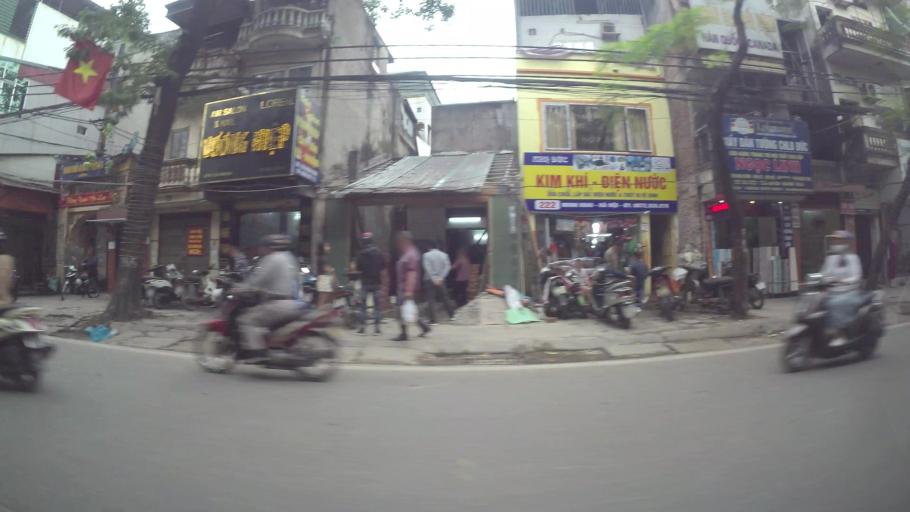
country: VN
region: Ha Noi
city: Hai BaTrung
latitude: 20.9952
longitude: 105.8548
